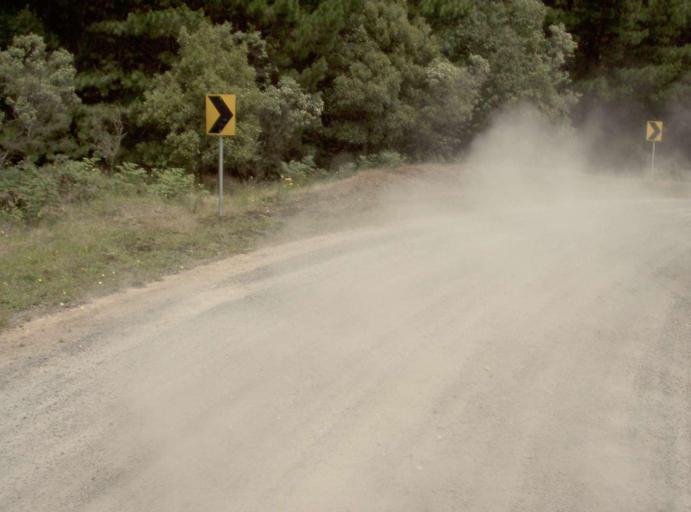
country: AU
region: Victoria
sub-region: Latrobe
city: Traralgon
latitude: -38.3808
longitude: 146.6676
